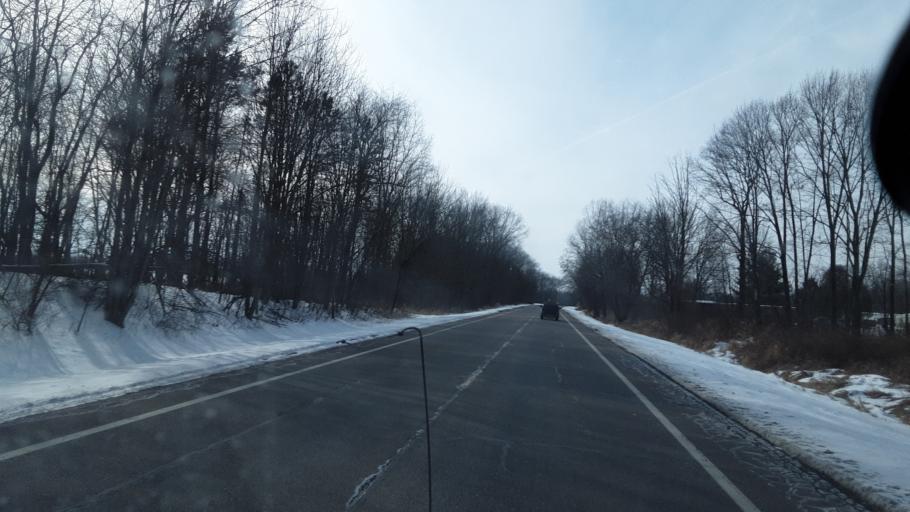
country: US
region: Ohio
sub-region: Stark County
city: Hartville
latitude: 41.0299
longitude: -81.2621
